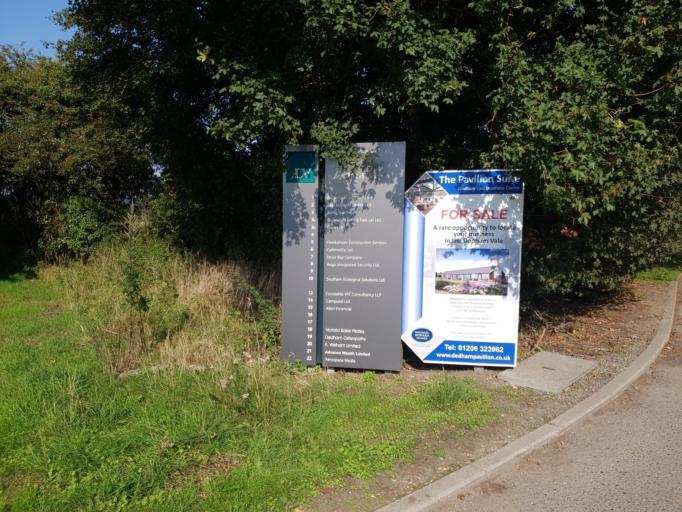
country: GB
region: England
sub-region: Suffolk
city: East Bergholt
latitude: 51.9517
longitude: 1.0135
